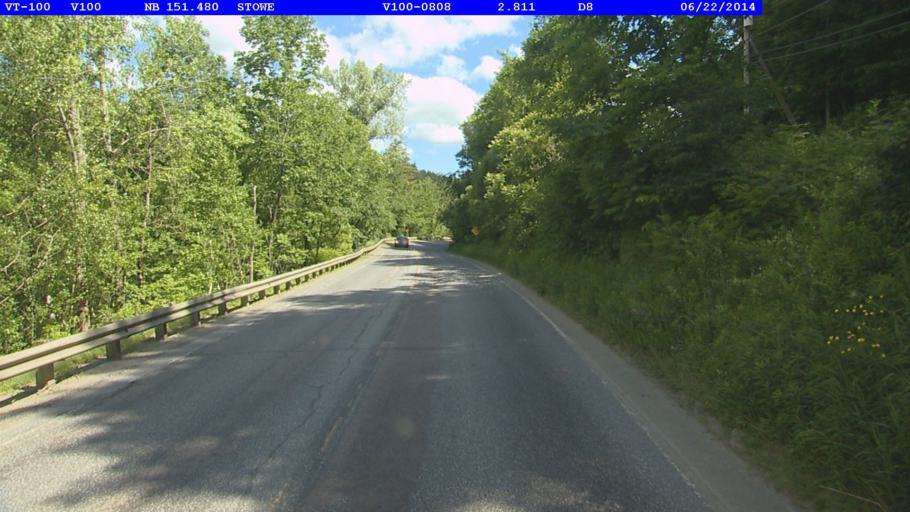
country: US
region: Vermont
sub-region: Lamoille County
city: Morristown
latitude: 44.4598
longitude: -72.6929
